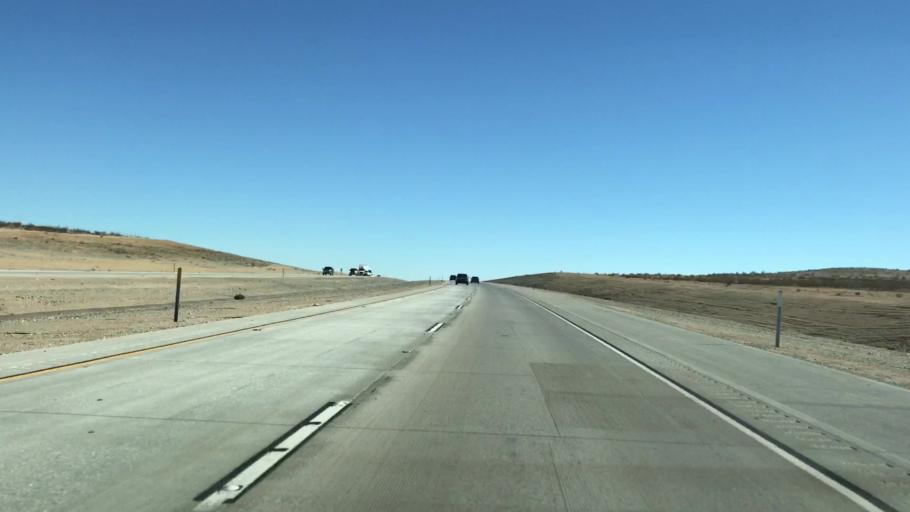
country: US
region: California
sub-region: San Bernardino County
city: Lenwood
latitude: 34.9156
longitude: -117.2386
